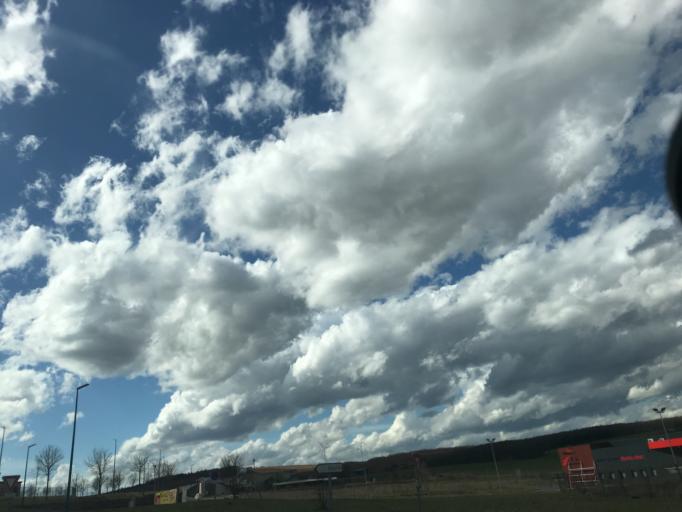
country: FR
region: Bourgogne
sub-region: Departement de la Nievre
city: Clamecy
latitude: 47.4742
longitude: 3.5185
